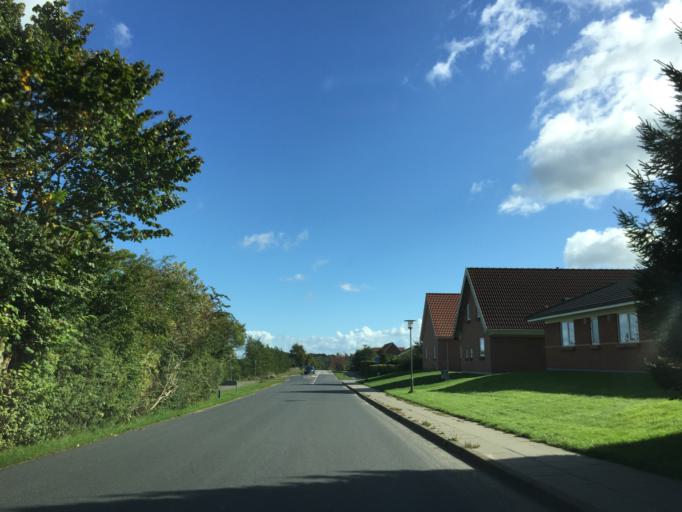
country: DK
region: Central Jutland
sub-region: Viborg Kommune
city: Viborg
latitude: 56.4458
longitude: 9.4416
